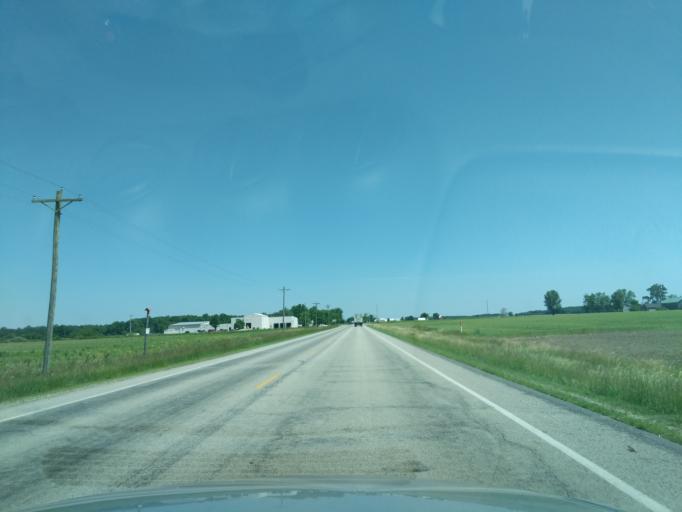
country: US
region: Indiana
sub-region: Huntington County
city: Huntington
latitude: 40.9587
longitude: -85.4713
